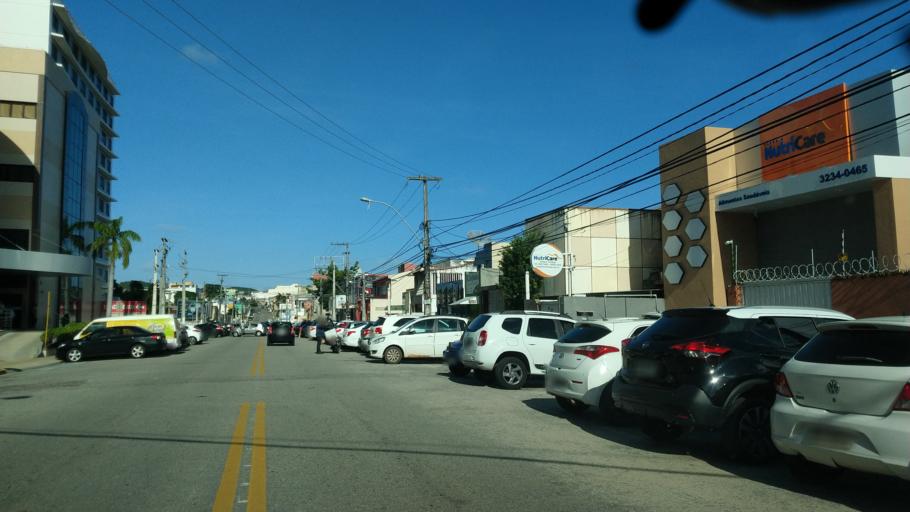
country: BR
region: Rio Grande do Norte
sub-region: Natal
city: Natal
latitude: -5.8243
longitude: -35.2074
